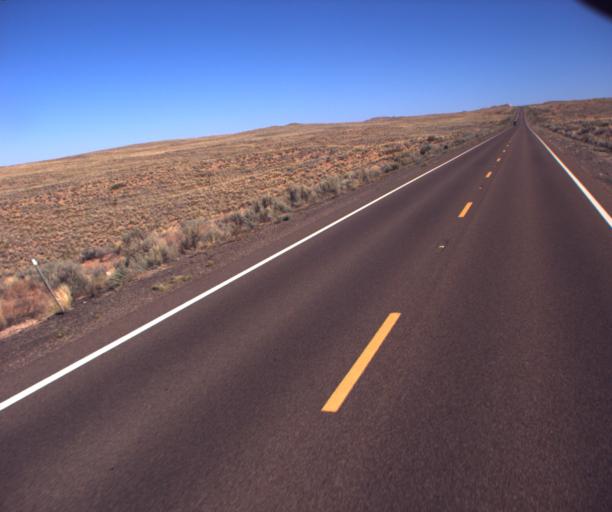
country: US
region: Arizona
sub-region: Navajo County
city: Winslow
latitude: 35.0564
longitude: -110.5898
